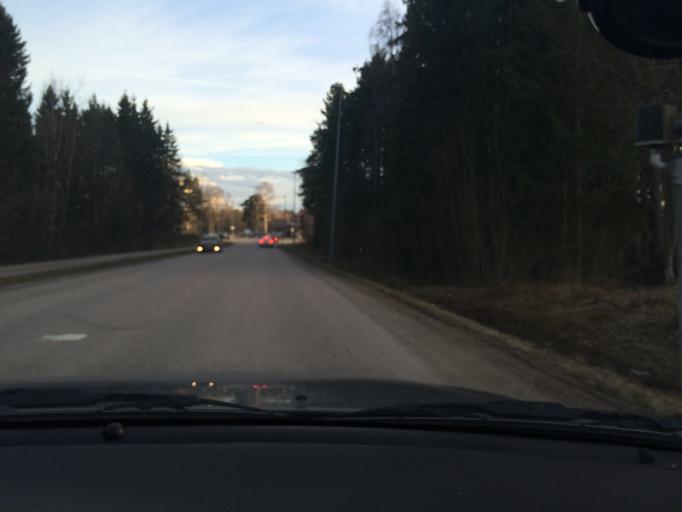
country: SE
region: Vaestmanland
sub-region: Vasteras
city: Vasteras
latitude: 59.6162
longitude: 16.5886
